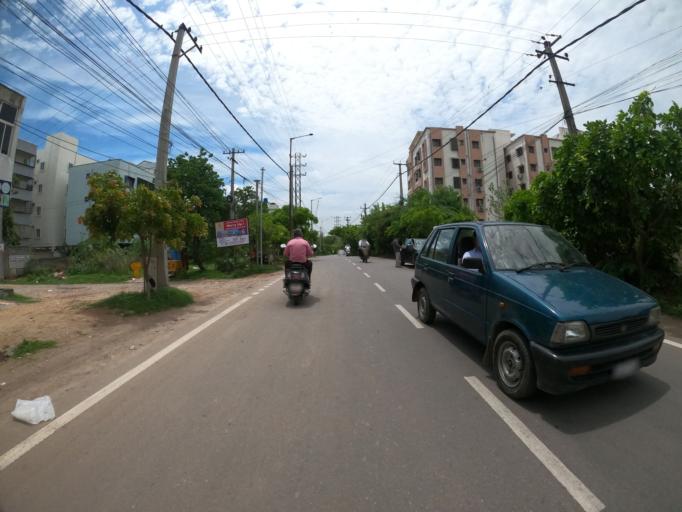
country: IN
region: Telangana
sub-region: Hyderabad
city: Hyderabad
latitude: 17.3658
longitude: 78.4159
